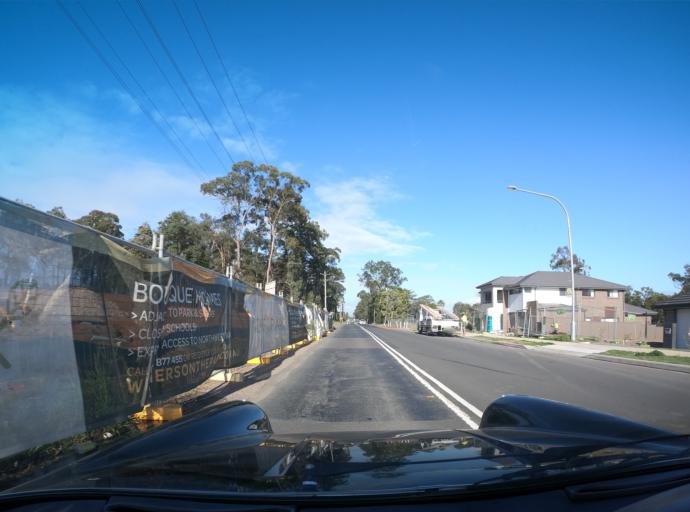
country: AU
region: New South Wales
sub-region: The Hills Shire
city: Beaumont Hills
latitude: -33.6845
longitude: 150.9549
